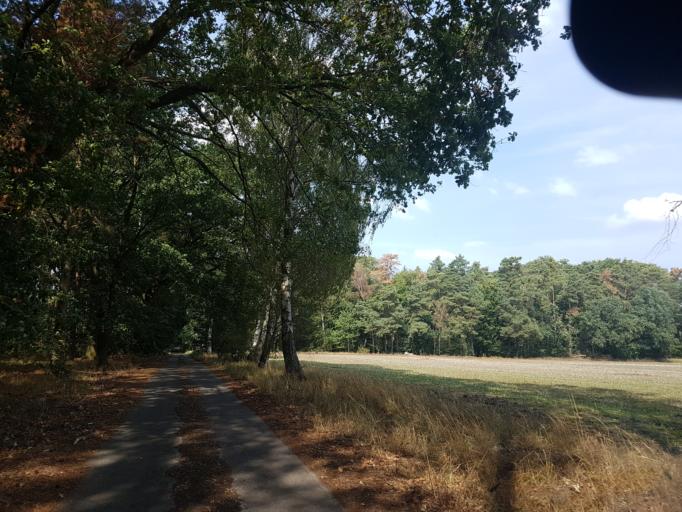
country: DE
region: Brandenburg
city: Gorzke
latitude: 52.0590
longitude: 12.2755
